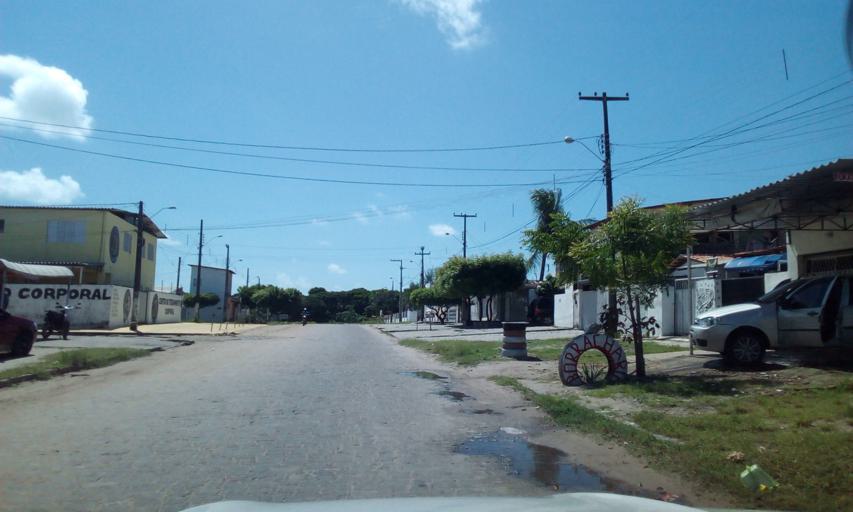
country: BR
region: Paraiba
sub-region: Joao Pessoa
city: Joao Pessoa
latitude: -7.1746
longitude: -34.8302
